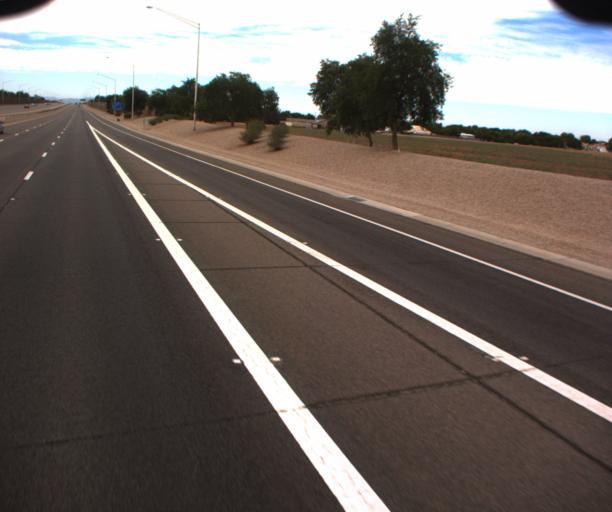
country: US
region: Arizona
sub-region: Maricopa County
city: Queen Creek
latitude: 33.3285
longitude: -111.6918
